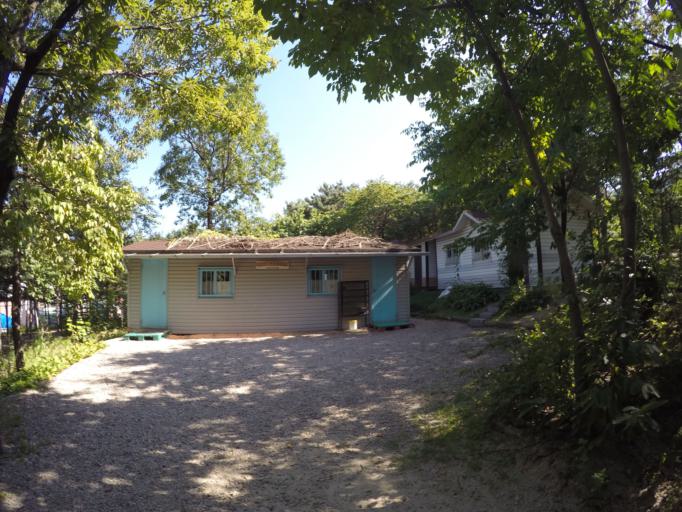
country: KR
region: Seoul
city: Seoul
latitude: 37.5582
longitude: 126.9948
